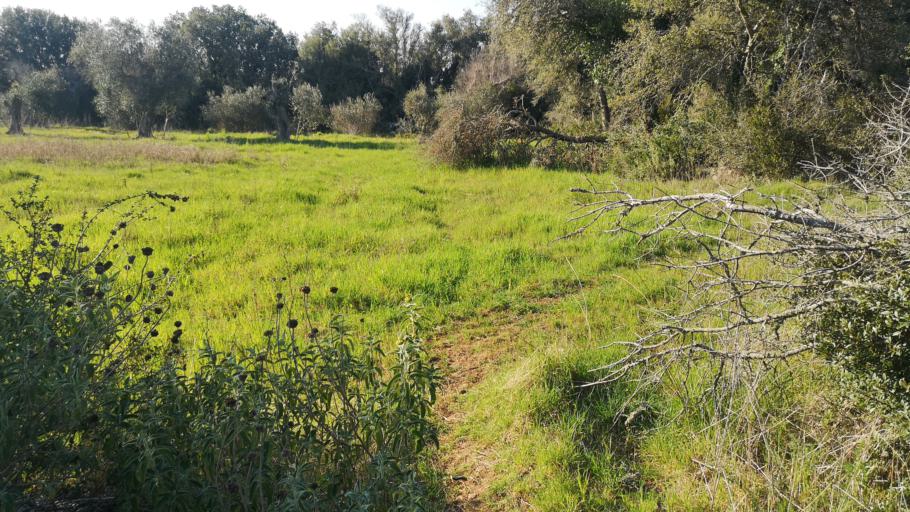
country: IT
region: Apulia
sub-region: Provincia di Lecce
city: Surano
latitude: 40.0058
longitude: 18.3372
